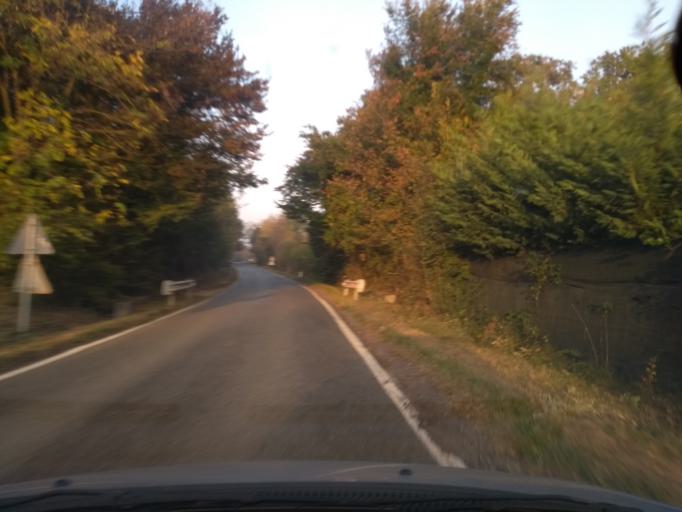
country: IT
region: Piedmont
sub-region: Provincia di Torino
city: La Cassa
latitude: 45.1737
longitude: 7.5096
